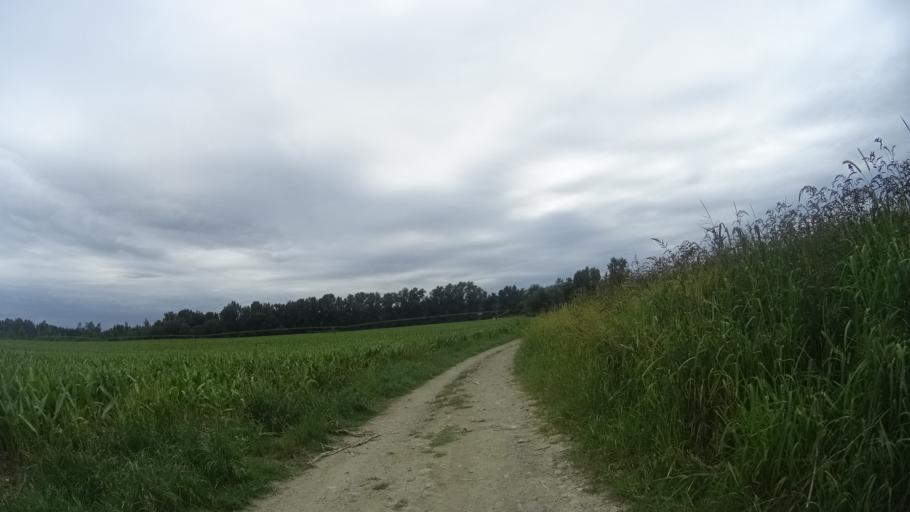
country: FR
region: Aquitaine
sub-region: Departement des Pyrenees-Atlantiques
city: Orthez
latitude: 43.4659
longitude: -0.7204
